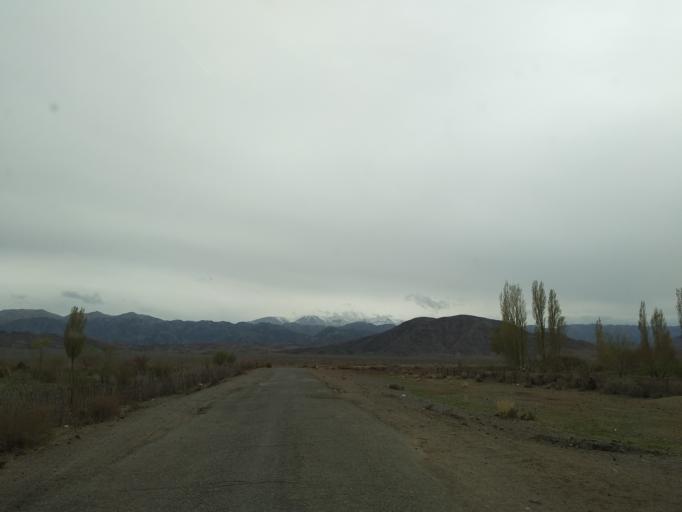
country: KG
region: Ysyk-Koel
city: Balykchy
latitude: 42.3208
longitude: 76.2345
